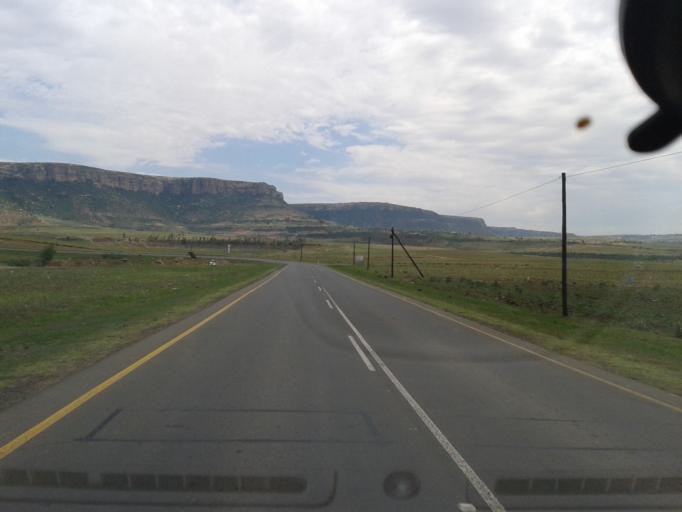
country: LS
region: Maseru
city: Maseru
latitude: -29.3524
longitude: 27.6119
